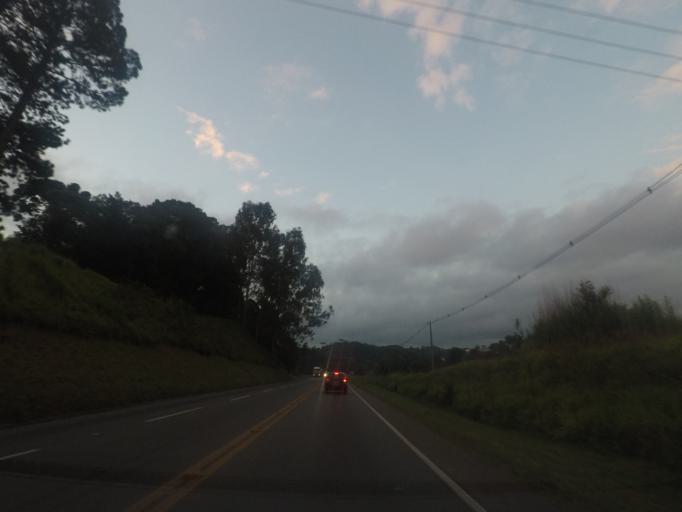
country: BR
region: Parana
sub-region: Almirante Tamandare
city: Almirante Tamandare
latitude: -25.3987
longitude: -49.3611
